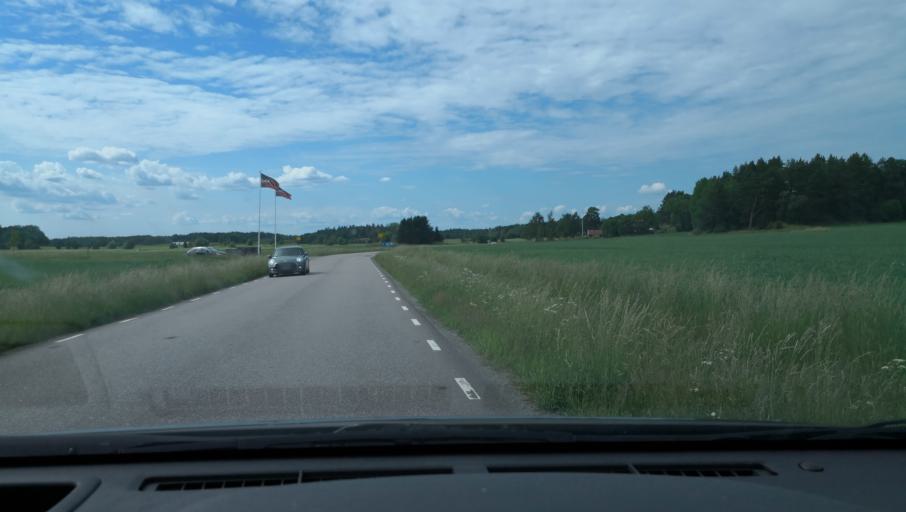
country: SE
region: Uppsala
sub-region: Uppsala Kommun
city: Uppsala
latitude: 59.8138
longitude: 17.5040
